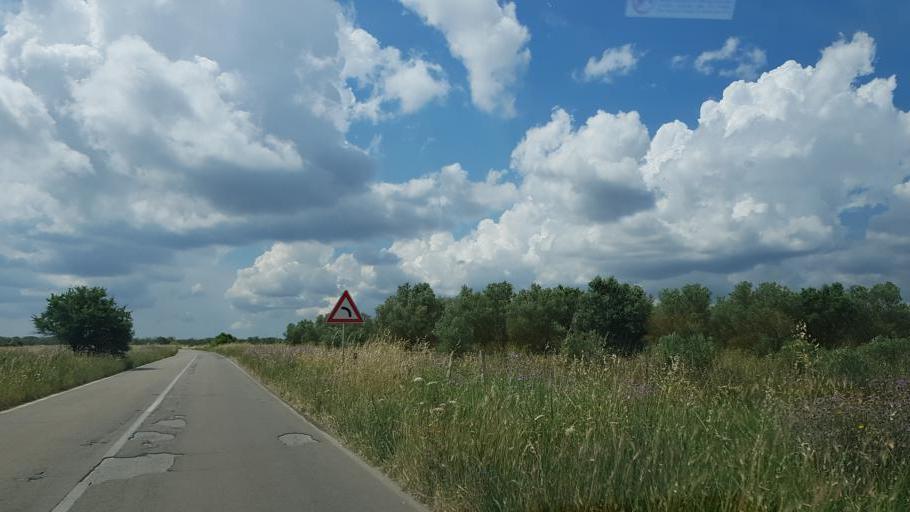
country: IT
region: Apulia
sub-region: Provincia di Brindisi
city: Mesagne
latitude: 40.5243
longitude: 17.8211
